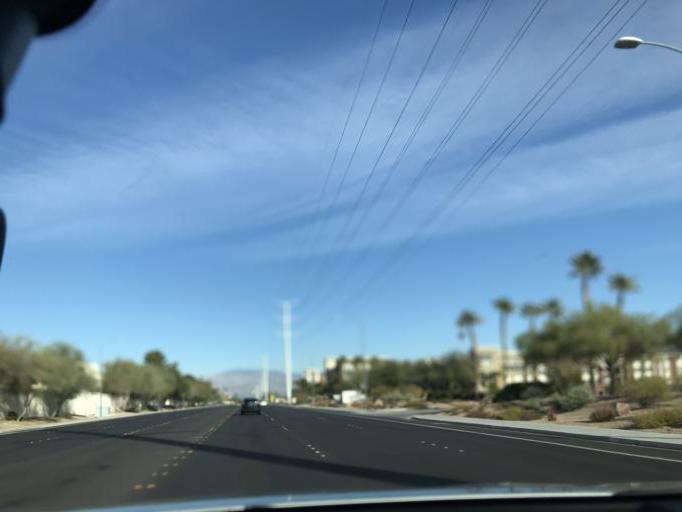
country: US
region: Nevada
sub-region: Clark County
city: Spring Valley
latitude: 36.2070
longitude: -115.2606
